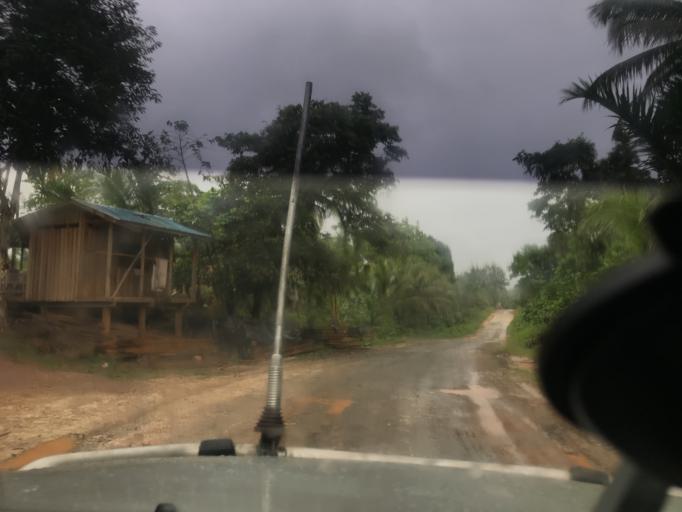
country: SB
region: Malaita
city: Auki
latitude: -9.0054
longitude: 160.7911
